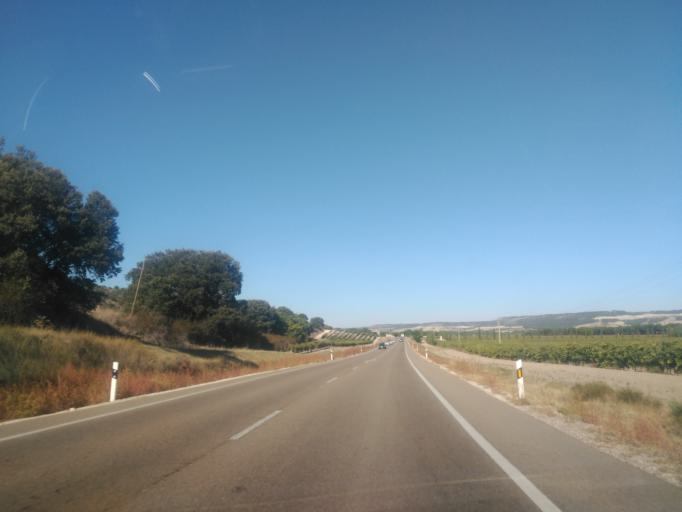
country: ES
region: Castille and Leon
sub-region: Provincia de Valladolid
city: Valbuena de Duero
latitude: 41.6254
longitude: -4.2762
